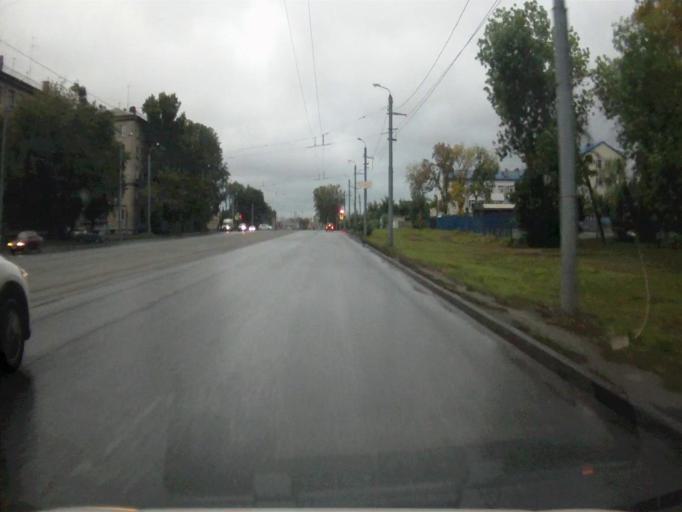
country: RU
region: Chelyabinsk
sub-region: Gorod Chelyabinsk
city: Chelyabinsk
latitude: 55.1590
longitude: 61.4448
